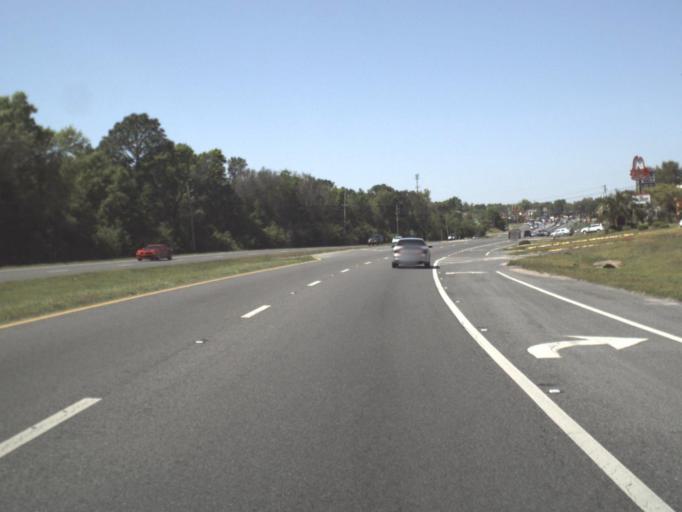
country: US
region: Florida
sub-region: Escambia County
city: Bellview
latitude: 30.4560
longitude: -87.2981
